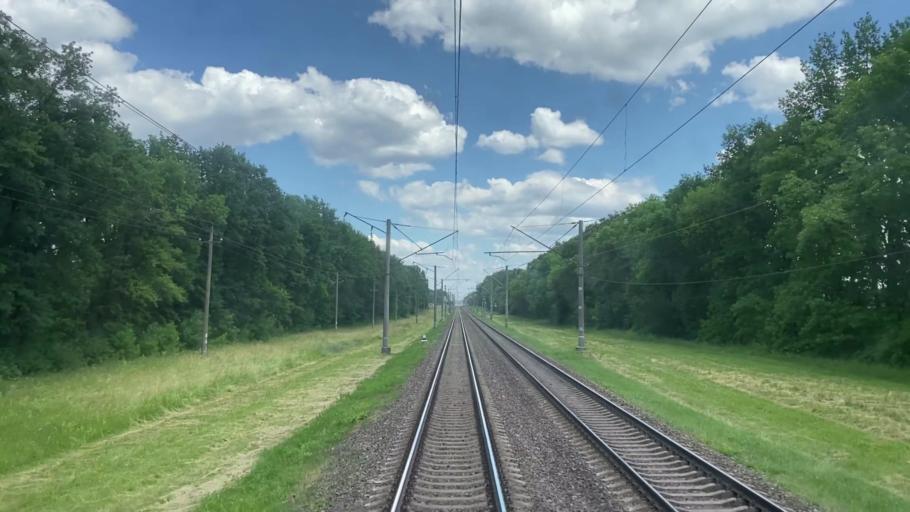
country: BY
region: Brest
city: Byaroza
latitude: 52.5429
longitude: 24.9489
